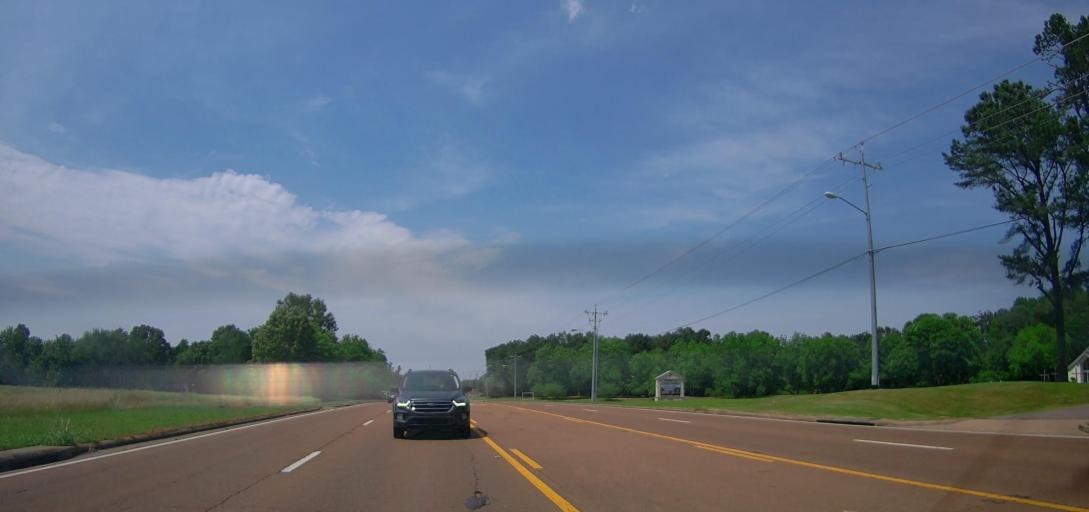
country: US
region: Mississippi
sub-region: De Soto County
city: Olive Branch
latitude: 34.9813
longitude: -89.8306
